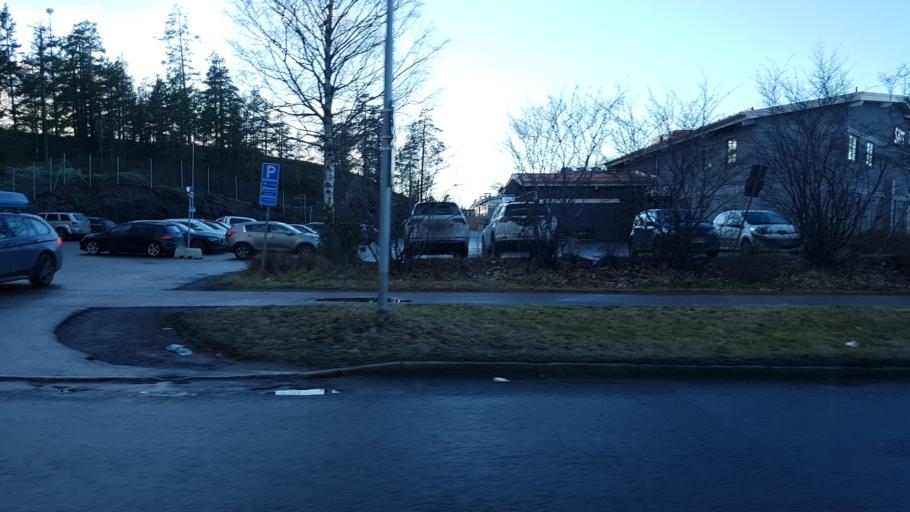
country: SE
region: Stockholm
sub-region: Tyreso Kommun
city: Bollmora
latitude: 59.2424
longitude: 18.2151
